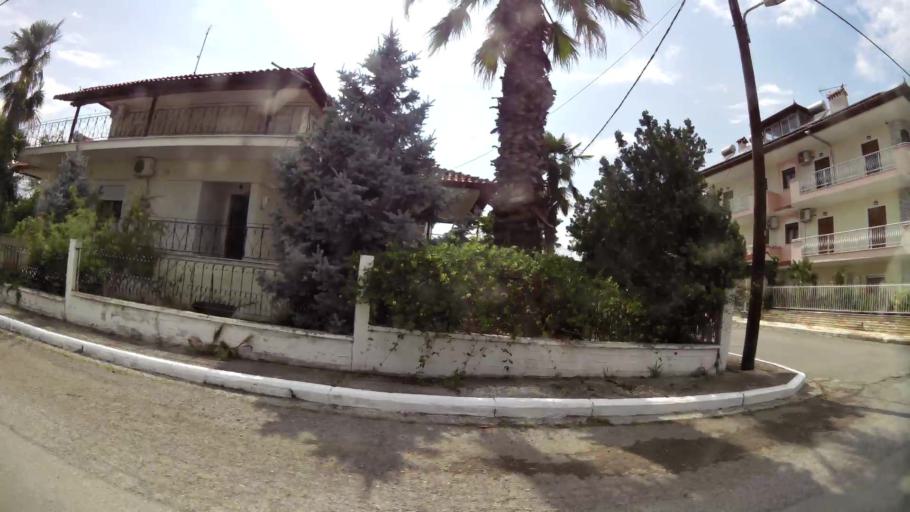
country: GR
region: Central Macedonia
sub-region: Nomos Pierias
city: Makrygialos
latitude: 40.4136
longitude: 22.6042
